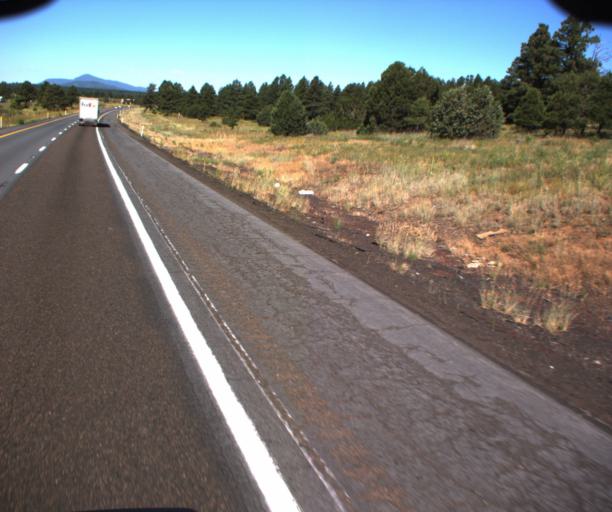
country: US
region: Arizona
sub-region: Coconino County
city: Parks
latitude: 35.2489
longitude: -111.9678
